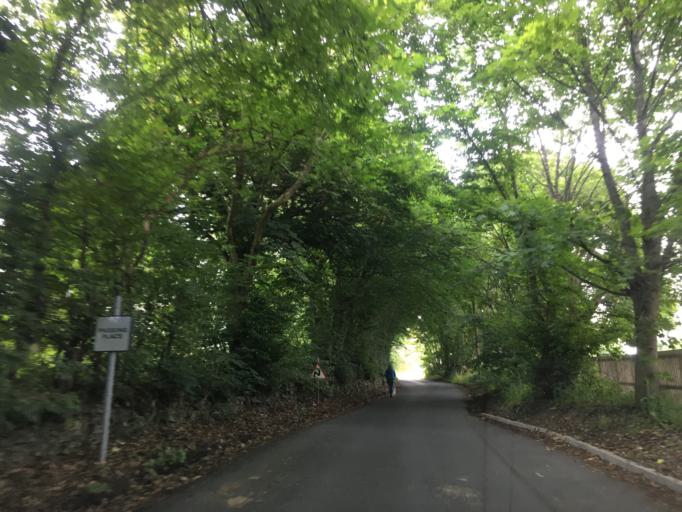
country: GB
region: Scotland
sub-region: The Scottish Borders
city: Peebles
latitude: 55.6612
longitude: -3.2013
